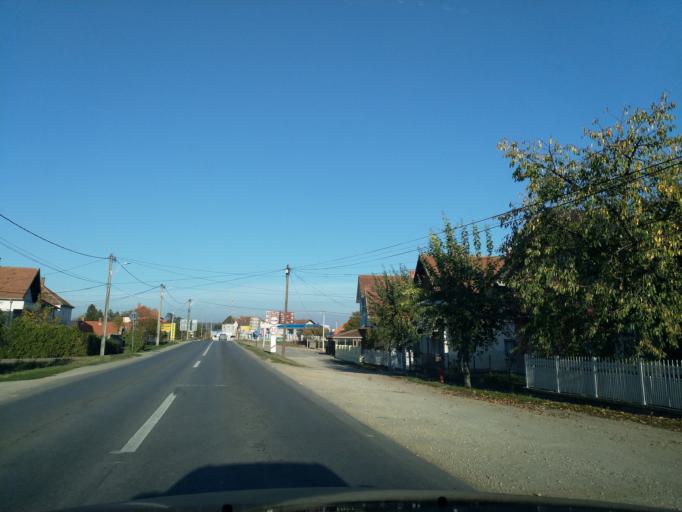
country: RS
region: Central Serbia
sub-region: Pomoravski Okrug
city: Svilajnac
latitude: 44.2323
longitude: 21.1842
